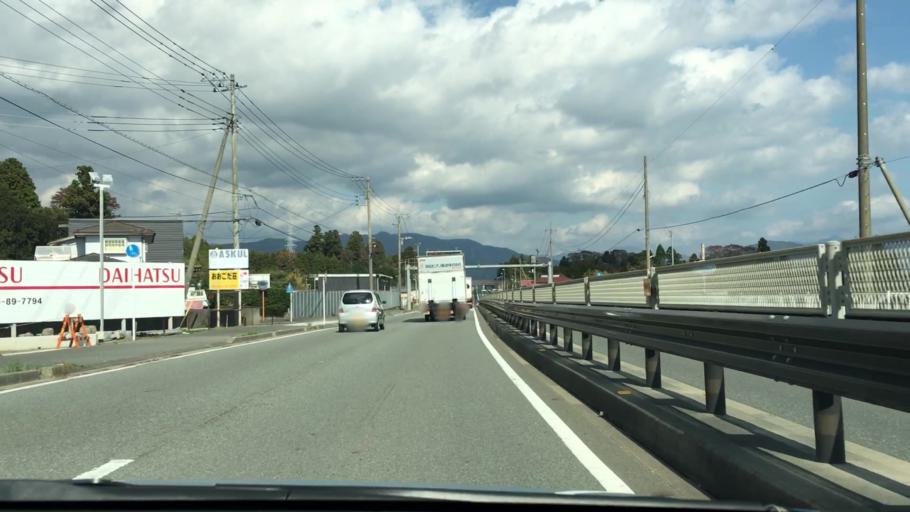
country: JP
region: Shizuoka
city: Gotemba
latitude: 35.3290
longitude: 138.9319
